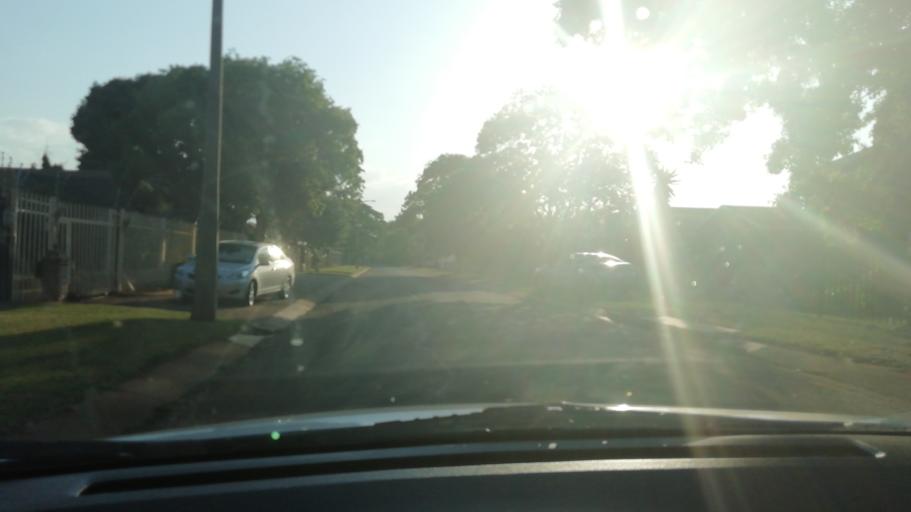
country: ZA
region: Gauteng
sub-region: Ekurhuleni Metropolitan Municipality
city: Benoni
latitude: -26.2012
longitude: 28.2949
